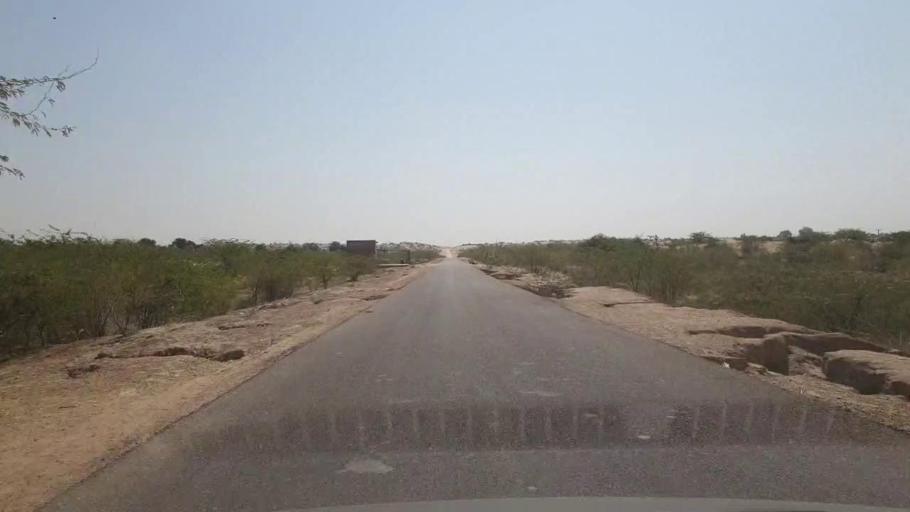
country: PK
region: Sindh
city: Chor
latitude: 25.5818
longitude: 70.1882
